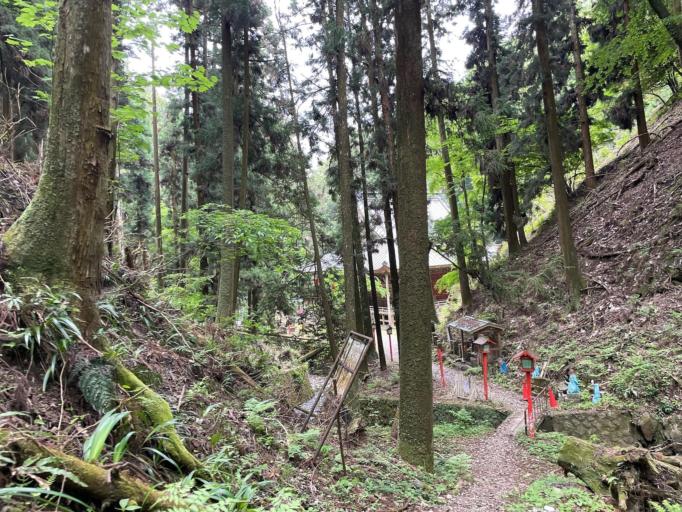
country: JP
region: Tochigi
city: Tanuma
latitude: 36.4761
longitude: 139.5888
